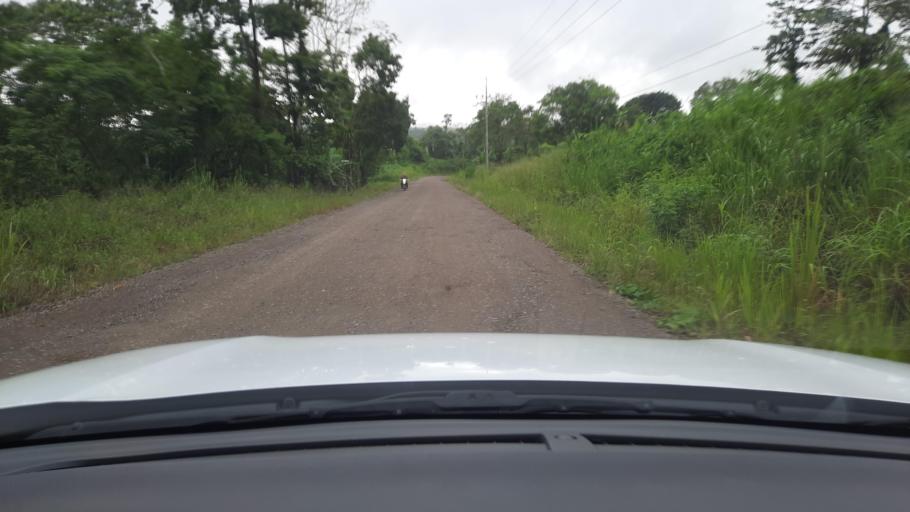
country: CR
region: Alajuela
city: San Jose
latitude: 11.0025
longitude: -85.3061
